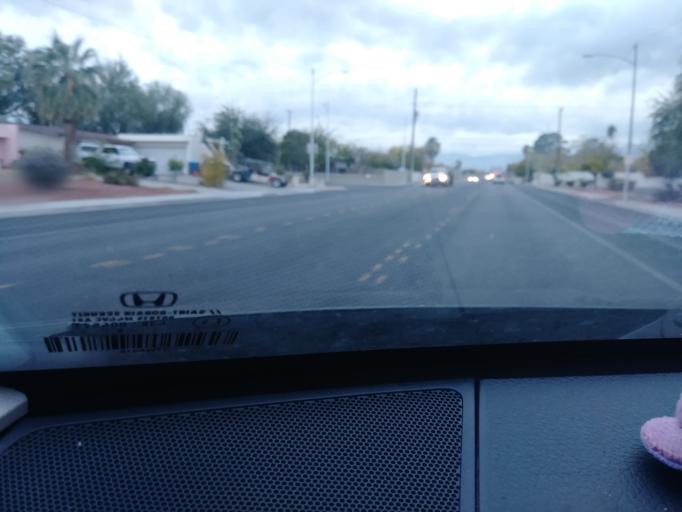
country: US
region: Nevada
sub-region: Clark County
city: Spring Valley
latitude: 36.1664
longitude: -115.2248
